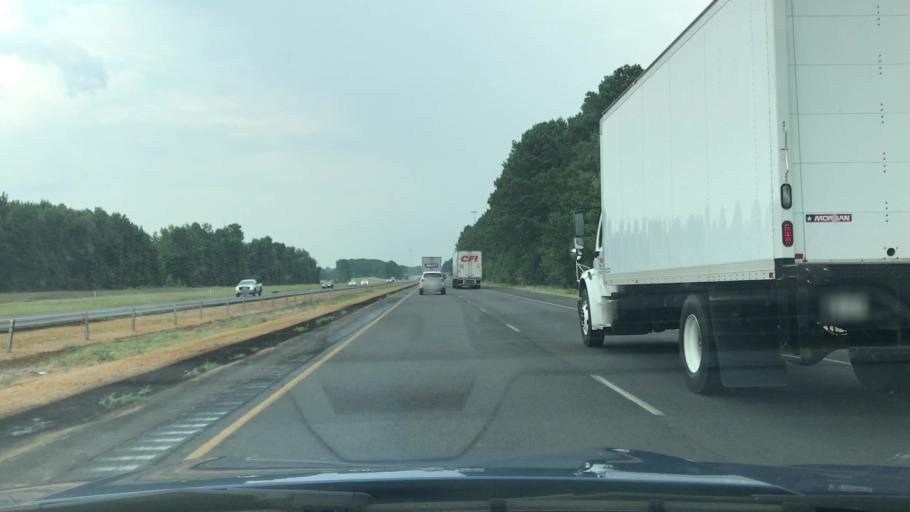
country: US
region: Texas
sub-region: Harrison County
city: Marshall
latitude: 32.4954
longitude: -94.2527
